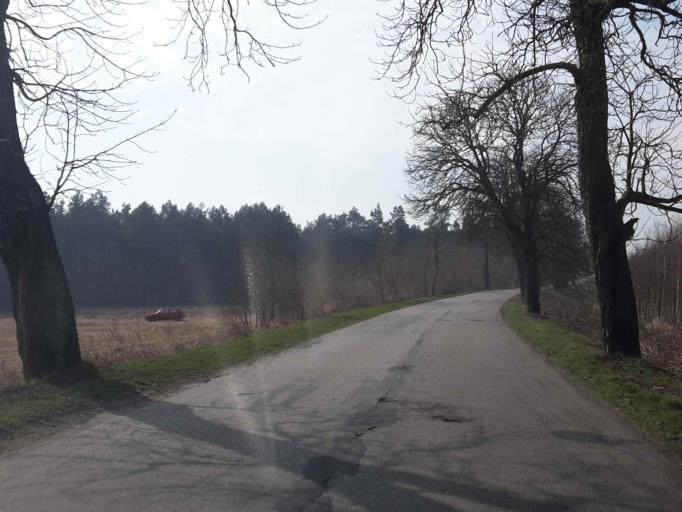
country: PL
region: Kujawsko-Pomorskie
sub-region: Powiat nakielski
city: Szubin
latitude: 53.0742
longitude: 17.7231
